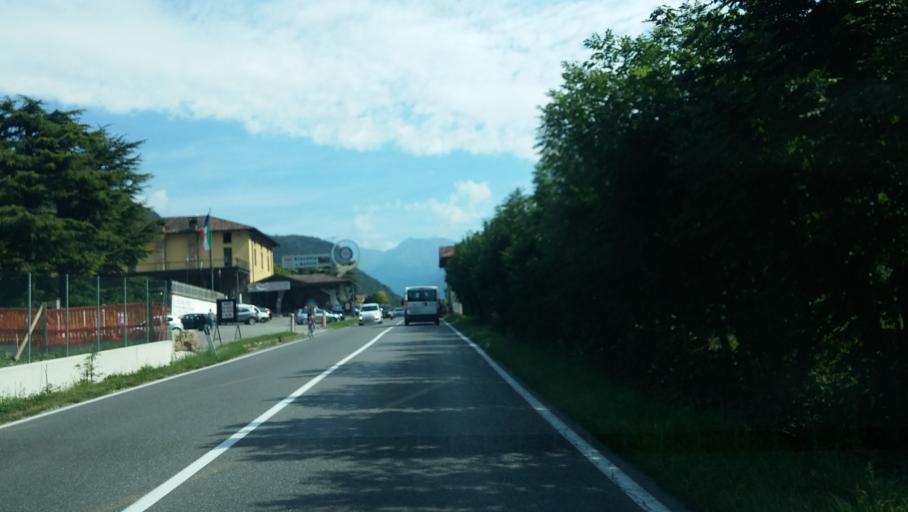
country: IT
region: Lombardy
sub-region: Provincia di Lecco
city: Ballabio
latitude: 45.9172
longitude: 9.4357
